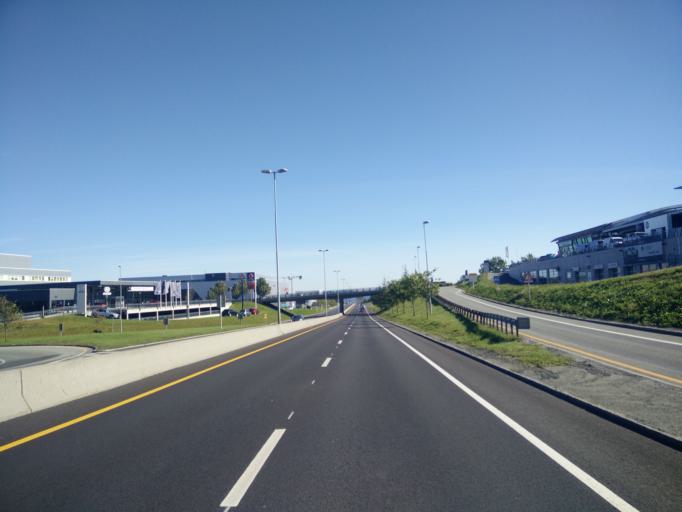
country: NO
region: Sor-Trondelag
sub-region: Trondheim
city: Trondheim
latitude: 63.4187
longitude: 10.4611
